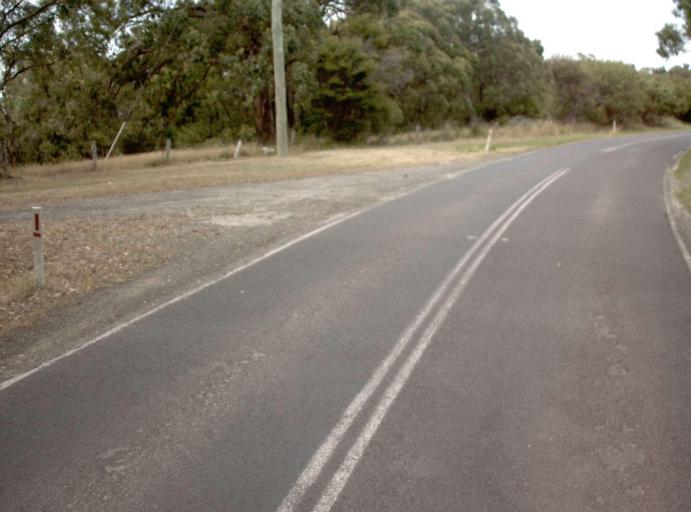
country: AU
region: Victoria
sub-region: Latrobe
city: Traralgon
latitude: -38.1296
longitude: 146.4728
